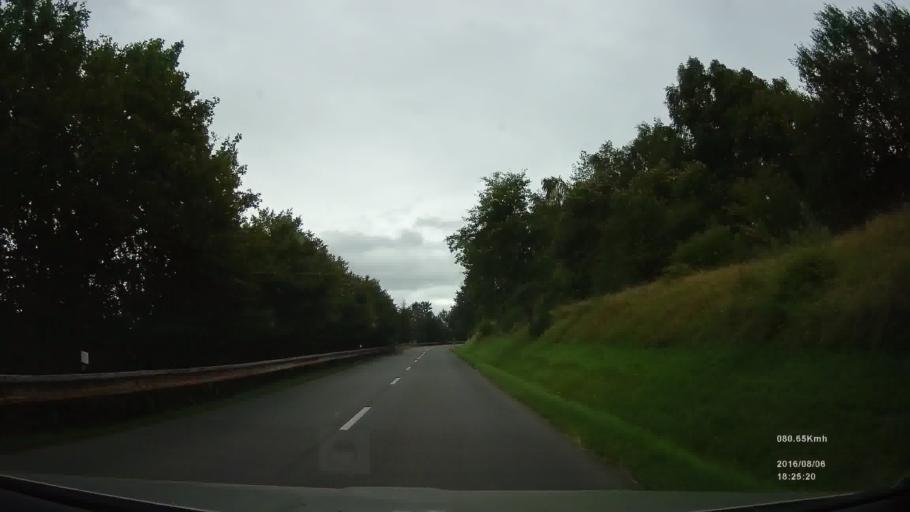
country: SK
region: Presovsky
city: Svidnik
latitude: 49.2909
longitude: 21.5736
